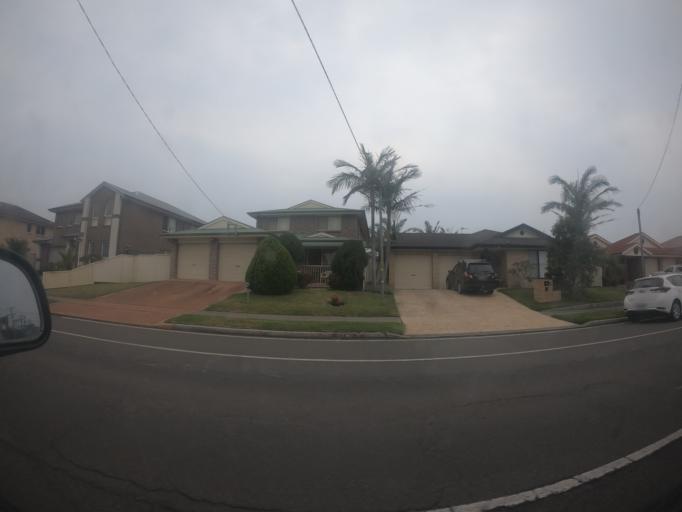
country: AU
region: New South Wales
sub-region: Shellharbour
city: Barrack Heights
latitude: -34.5645
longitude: 150.8630
